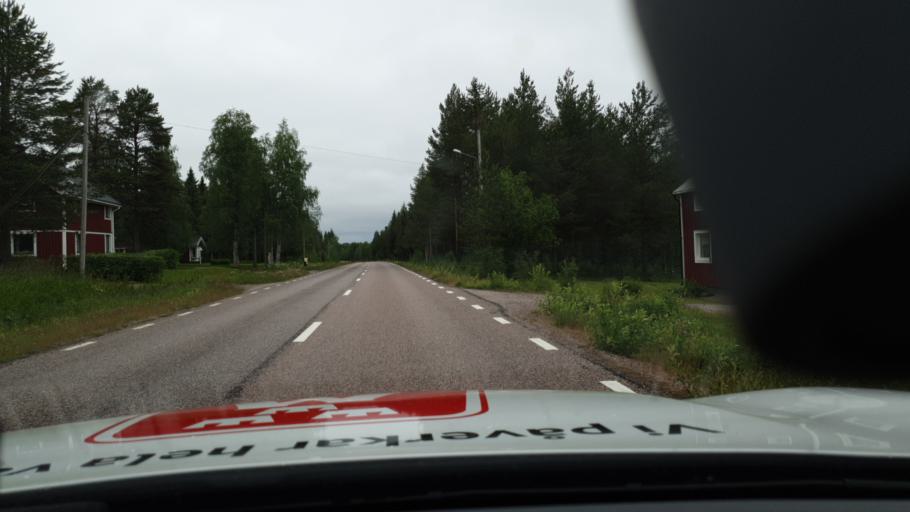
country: FI
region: Lapland
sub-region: Tunturi-Lappi
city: Kolari
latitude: 67.0568
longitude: 23.6761
